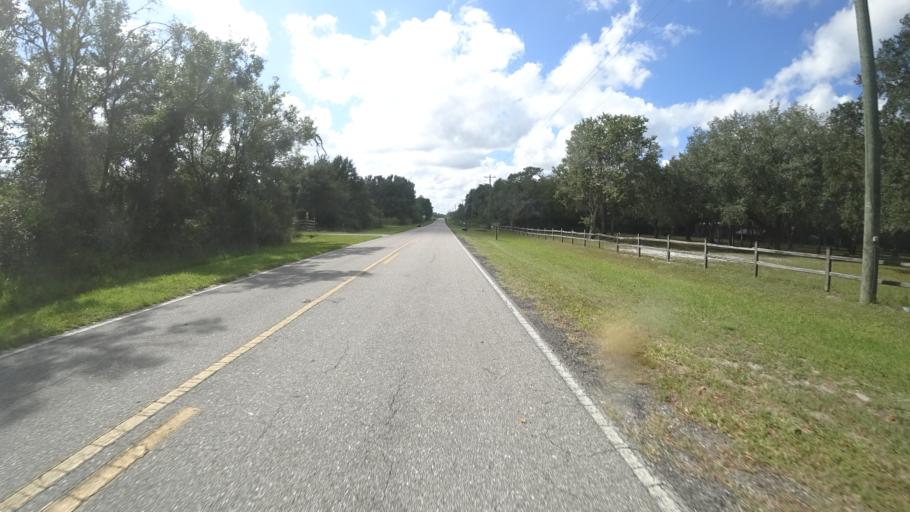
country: US
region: Florida
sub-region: Hillsborough County
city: Wimauma
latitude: 27.4391
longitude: -82.1286
